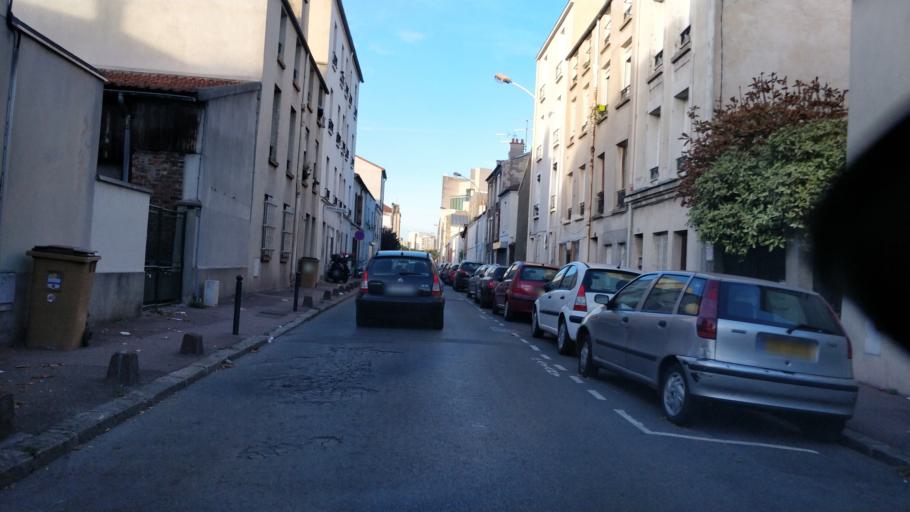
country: FR
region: Ile-de-France
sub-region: Departement du Val-de-Marne
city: Gentilly
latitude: 48.8142
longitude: 2.3432
